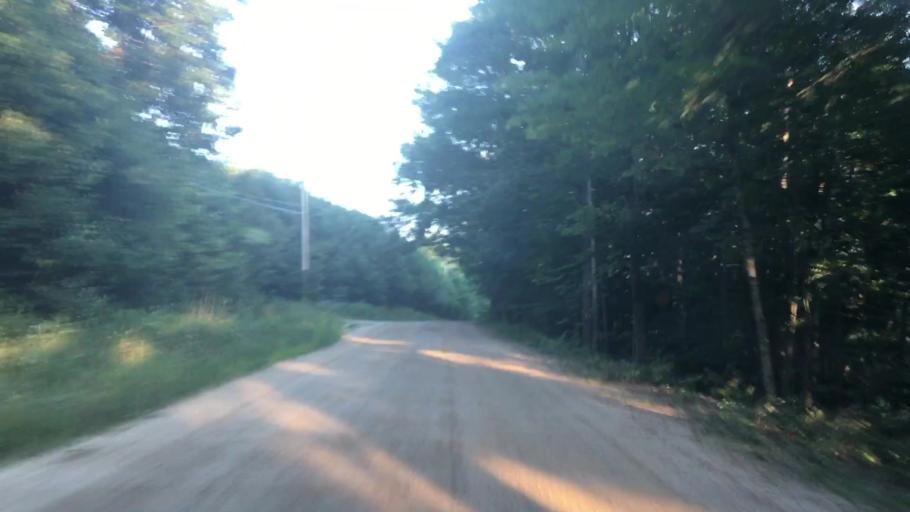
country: US
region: New Hampshire
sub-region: Belknap County
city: Barnstead
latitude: 43.4057
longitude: -71.2660
